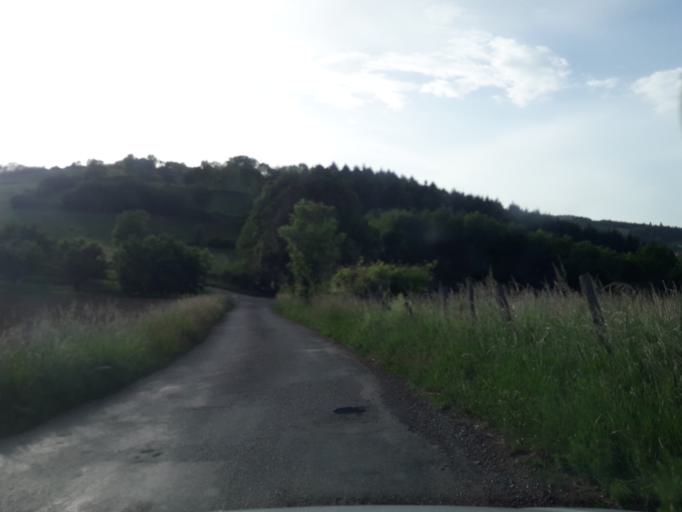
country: FR
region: Rhone-Alpes
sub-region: Departement du Rhone
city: Bessenay
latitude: 45.7537
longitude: 4.5274
